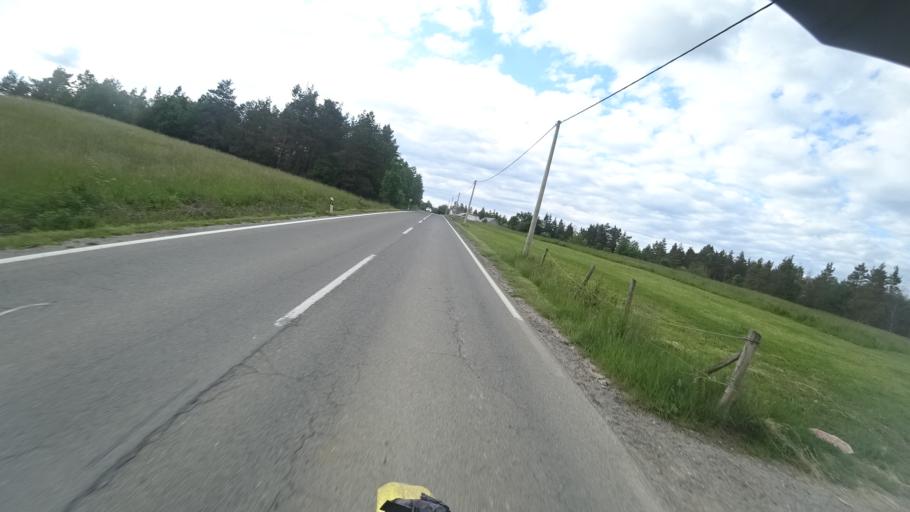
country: HR
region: Licko-Senjska
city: Gospic
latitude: 44.5202
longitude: 15.4154
